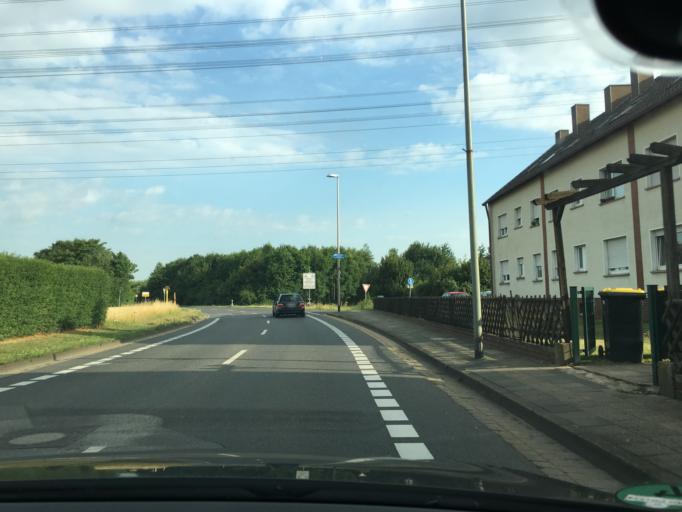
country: DE
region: North Rhine-Westphalia
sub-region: Regierungsbezirk Koln
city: Niederzier
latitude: 50.8336
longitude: 6.4410
